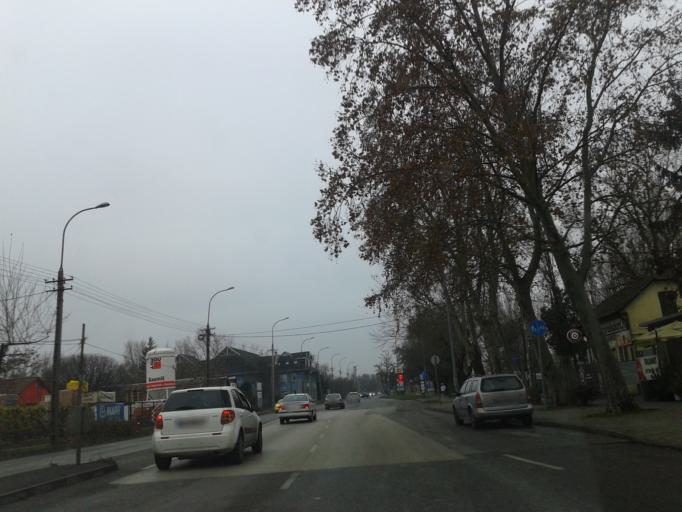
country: HU
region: Budapest
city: Budapest XXI. keruelet
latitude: 47.4129
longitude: 19.0579
